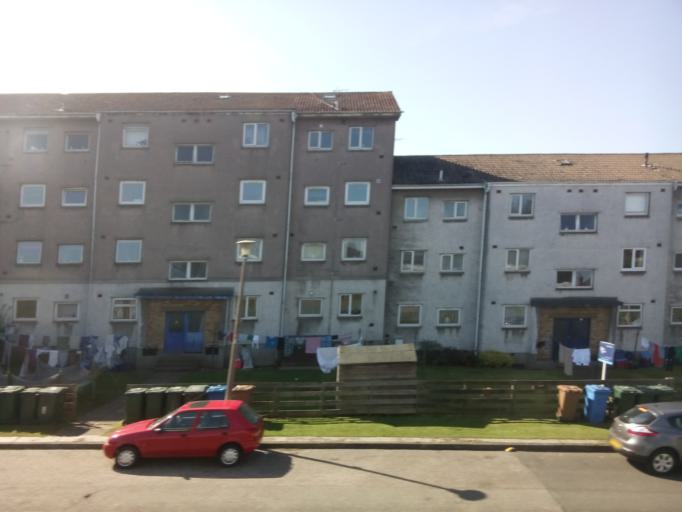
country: GB
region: Scotland
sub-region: Edinburgh
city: Colinton
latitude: 55.9325
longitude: -3.2792
